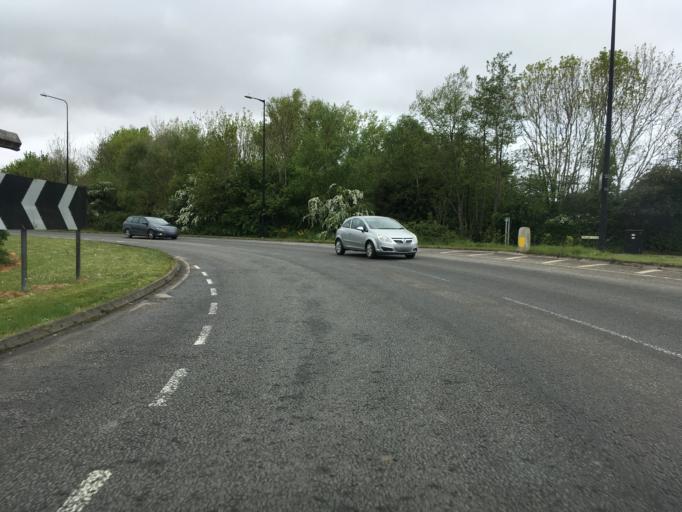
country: GB
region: England
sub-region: North Somerset
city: Hutton
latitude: 51.3451
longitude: -2.9314
